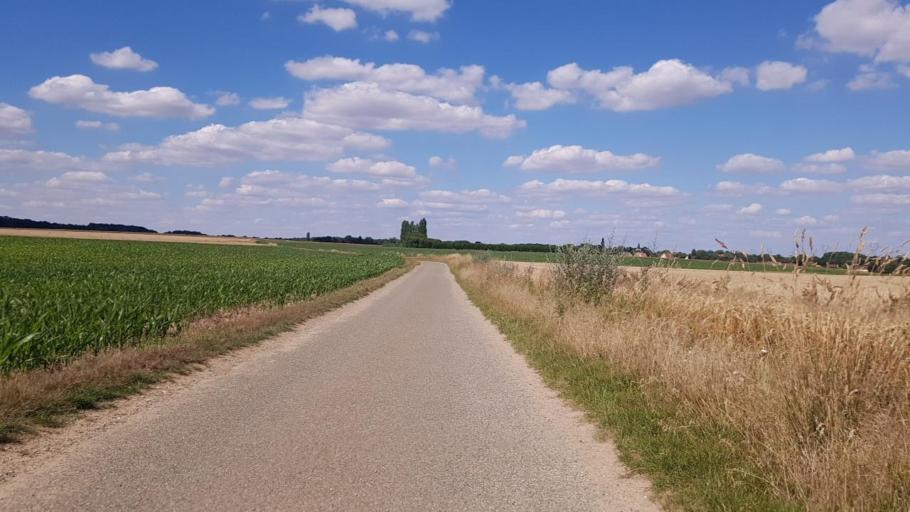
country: FR
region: Picardie
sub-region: Departement de l'Oise
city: Ver-sur-Launette
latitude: 49.0976
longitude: 2.6758
